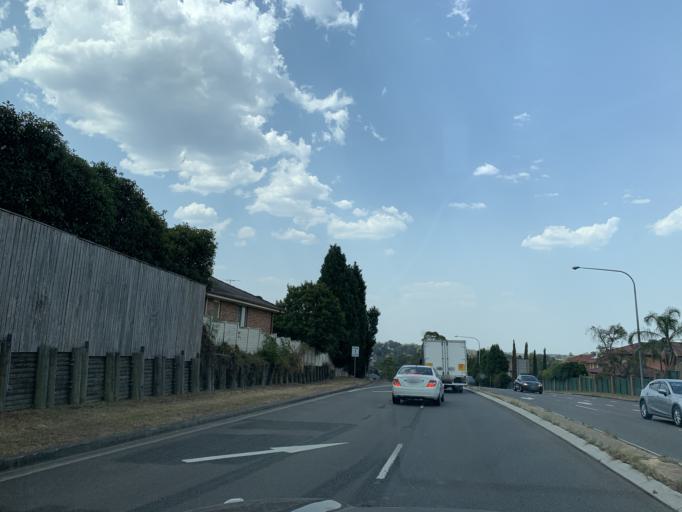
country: AU
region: New South Wales
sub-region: The Hills Shire
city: West Pennant
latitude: -33.7325
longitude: 151.0276
